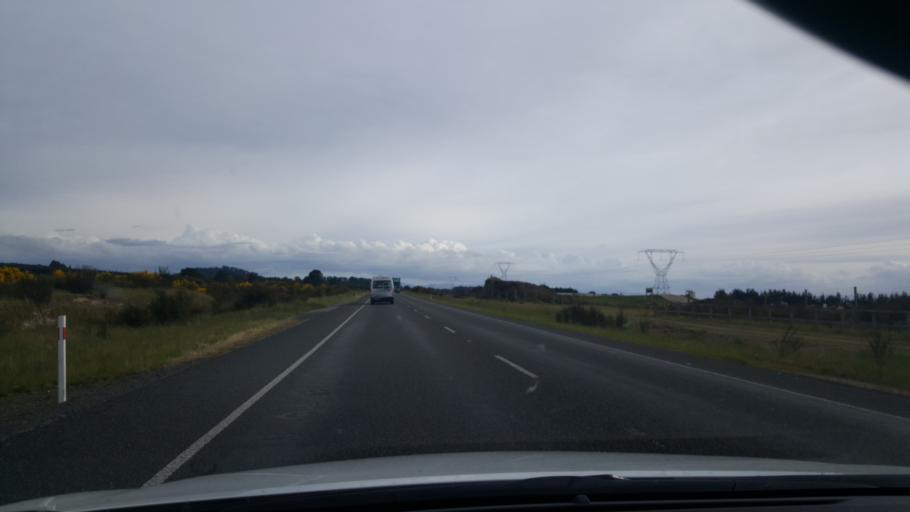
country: NZ
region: Waikato
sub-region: Taupo District
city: Taupo
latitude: -38.6888
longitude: 176.1139
